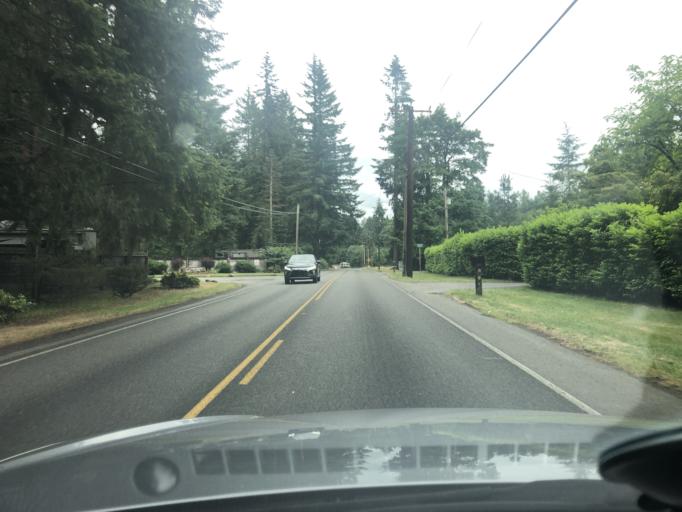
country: US
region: Washington
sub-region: King County
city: Black Diamond
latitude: 47.3309
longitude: -122.0446
